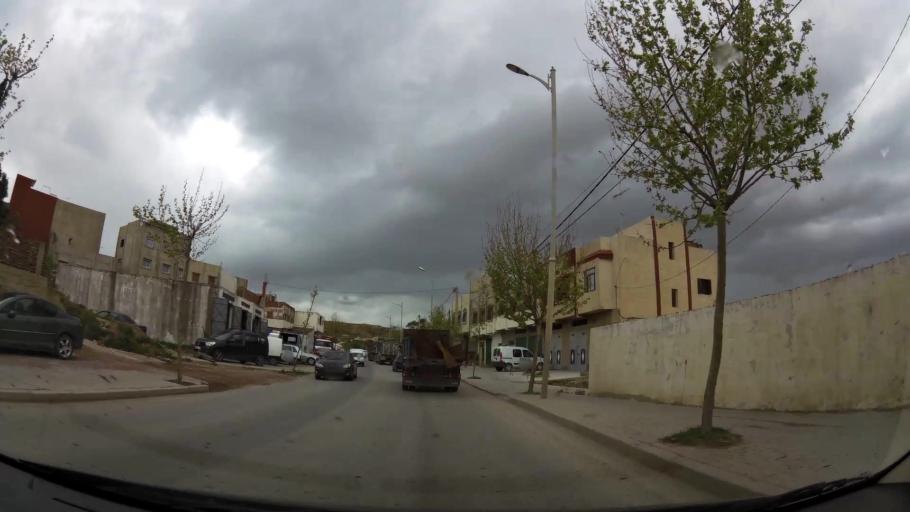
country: MA
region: Tanger-Tetouan
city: Tetouan
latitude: 35.5554
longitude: -5.4004
